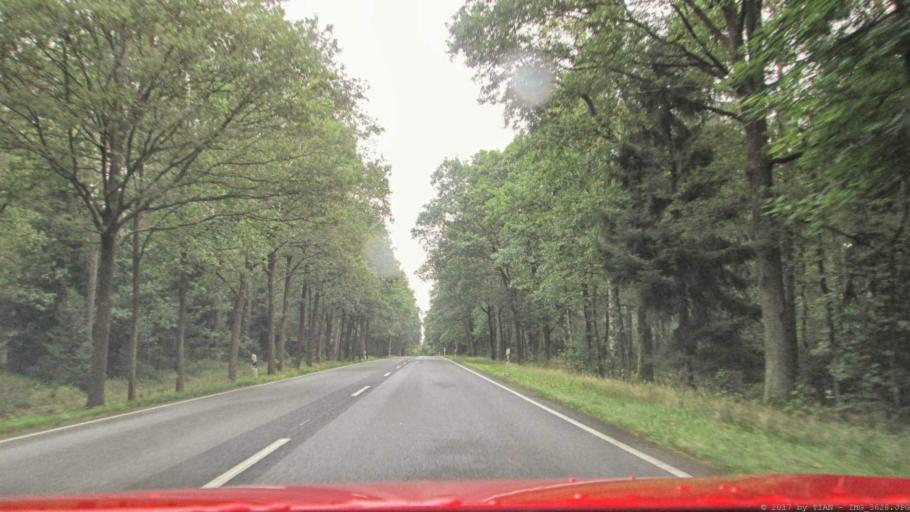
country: DE
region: Lower Saxony
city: Sprakensehl
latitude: 52.7367
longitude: 10.4867
